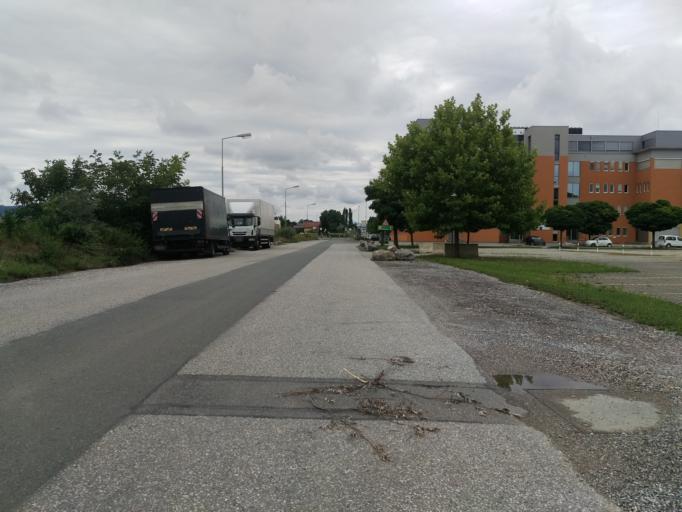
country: AT
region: Styria
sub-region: Politischer Bezirk Graz-Umgebung
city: Raaba
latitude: 47.0436
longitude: 15.4787
